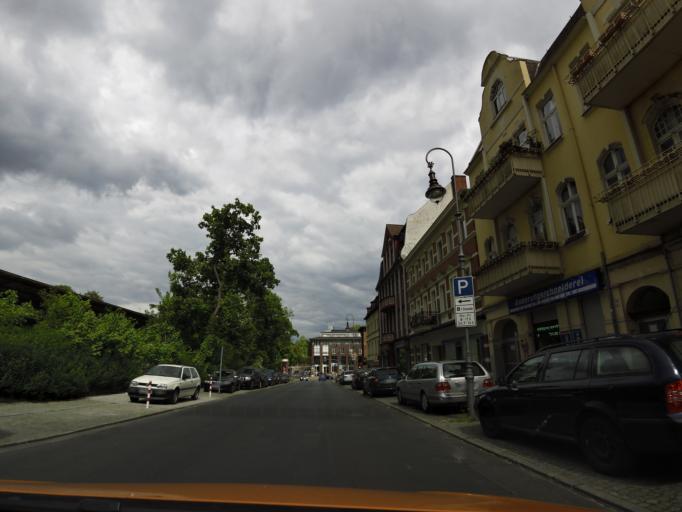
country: DE
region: Berlin
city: Zehlendorf Bezirk
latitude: 52.4304
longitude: 13.2580
